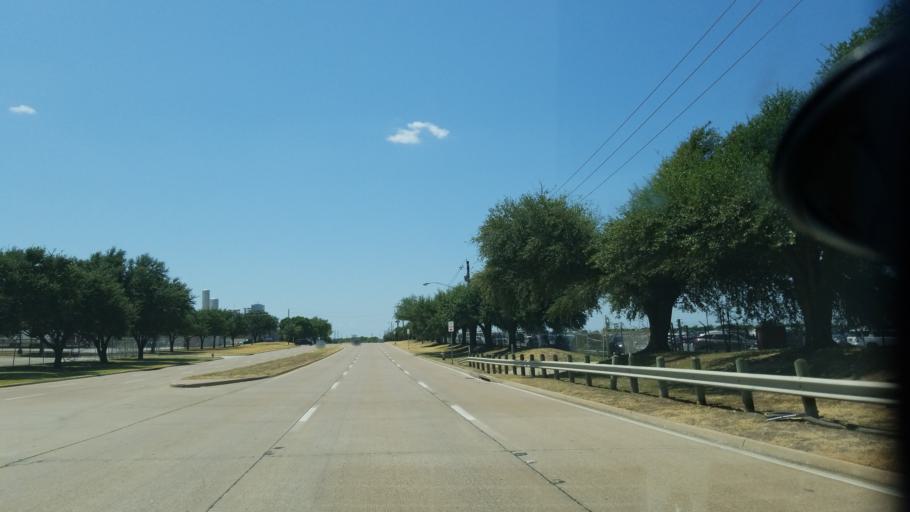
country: US
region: Texas
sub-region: Dallas County
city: Cockrell Hill
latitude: 32.7058
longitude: -96.9155
